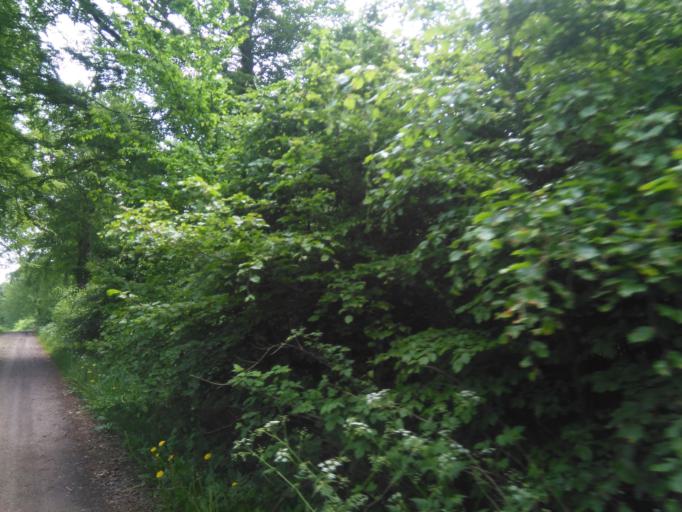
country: DK
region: Central Jutland
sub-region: Favrskov Kommune
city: Hinnerup
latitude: 56.2726
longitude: 10.0131
